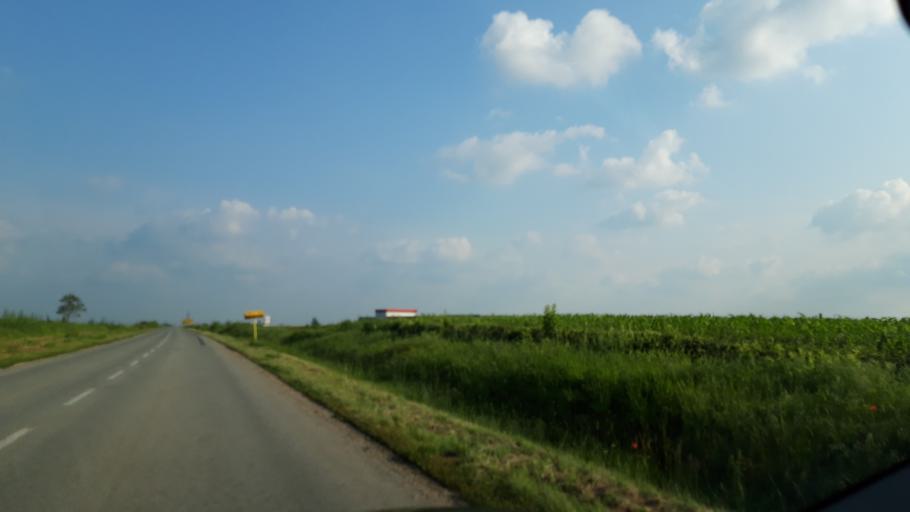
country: RS
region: Autonomna Pokrajina Vojvodina
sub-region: Sremski Okrug
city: Ingija
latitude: 45.0689
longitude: 20.1265
